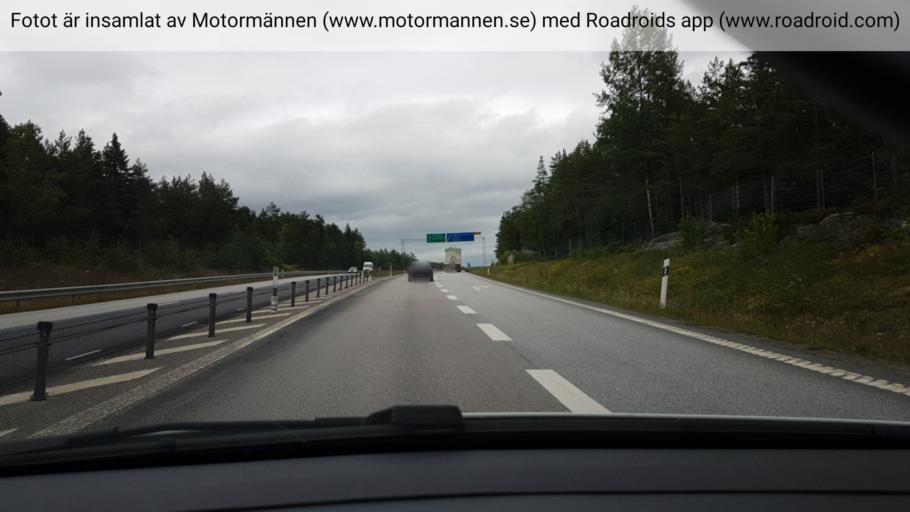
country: SE
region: Stockholm
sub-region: Norrtalje Kommun
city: Rimbo
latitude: 59.6322
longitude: 18.3225
